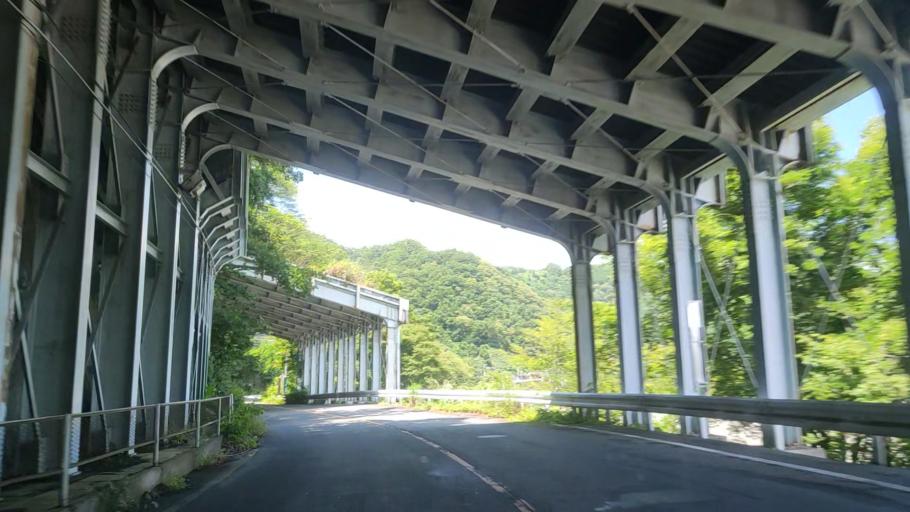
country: JP
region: Yamanashi
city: Ryuo
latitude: 35.4964
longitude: 138.4484
